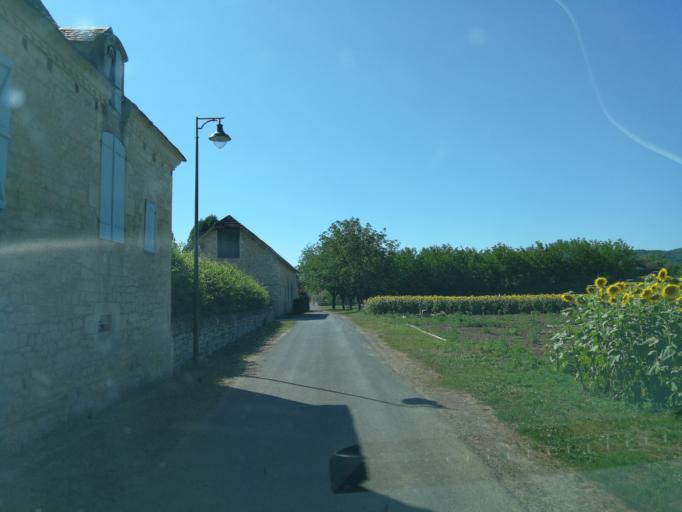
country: FR
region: Midi-Pyrenees
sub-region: Departement du Lot
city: Souillac
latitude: 44.8688
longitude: 1.4381
